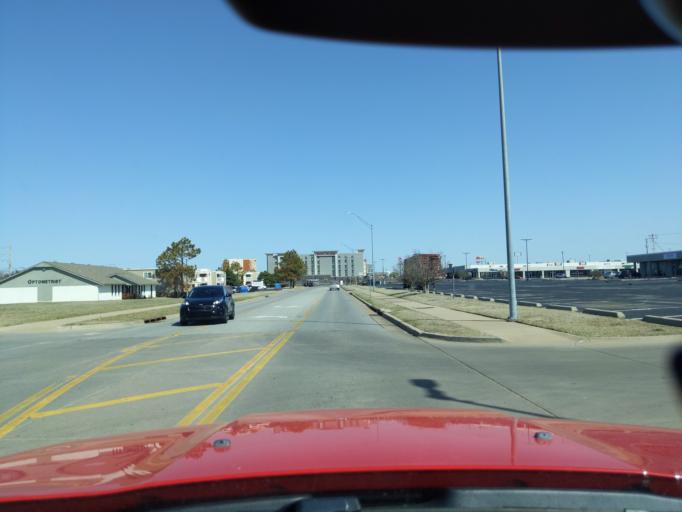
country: US
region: Oklahoma
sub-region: Cleveland County
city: Moore
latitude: 35.3438
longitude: -97.4970
